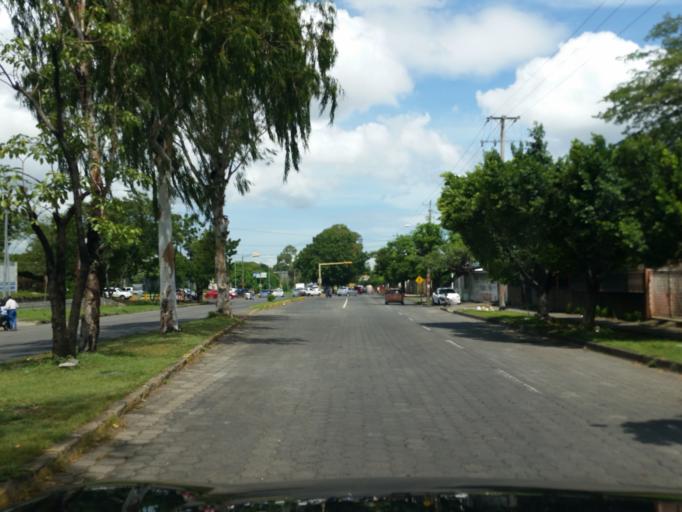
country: NI
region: Managua
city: Managua
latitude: 12.1278
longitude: -86.2432
